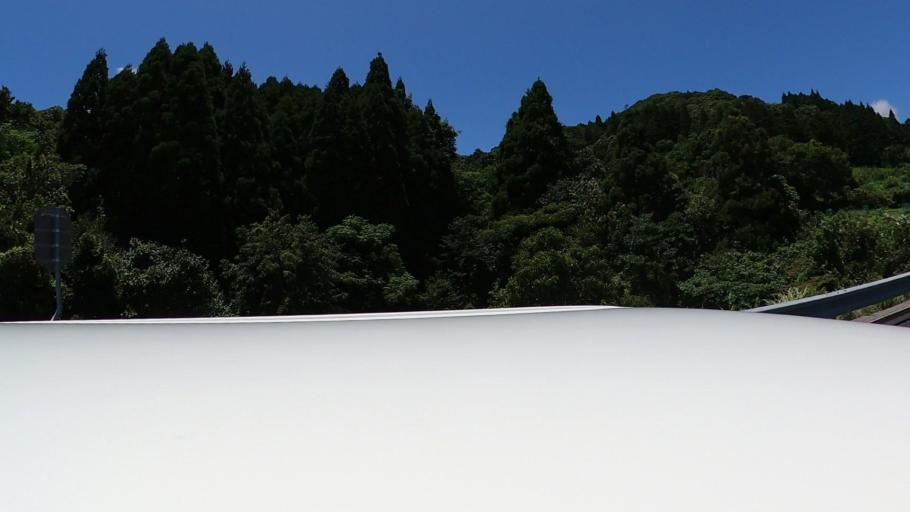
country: JP
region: Miyazaki
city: Nobeoka
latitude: 32.4039
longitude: 131.6148
